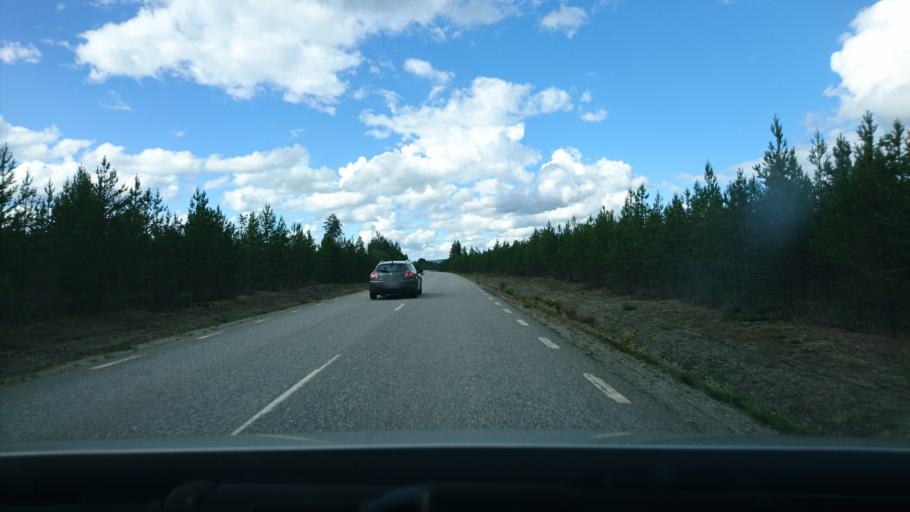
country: SE
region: Vaesterbotten
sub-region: Asele Kommun
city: Asele
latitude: 63.9582
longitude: 17.2700
